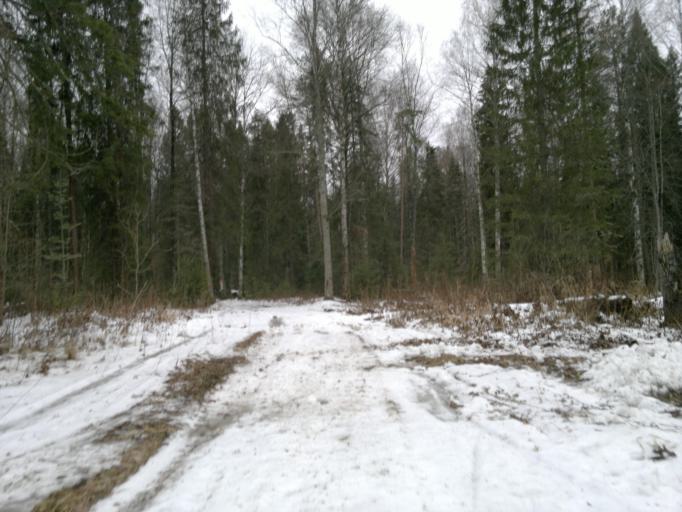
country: RU
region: Mariy-El
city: Yoshkar-Ola
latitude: 56.5949
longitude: 47.9685
